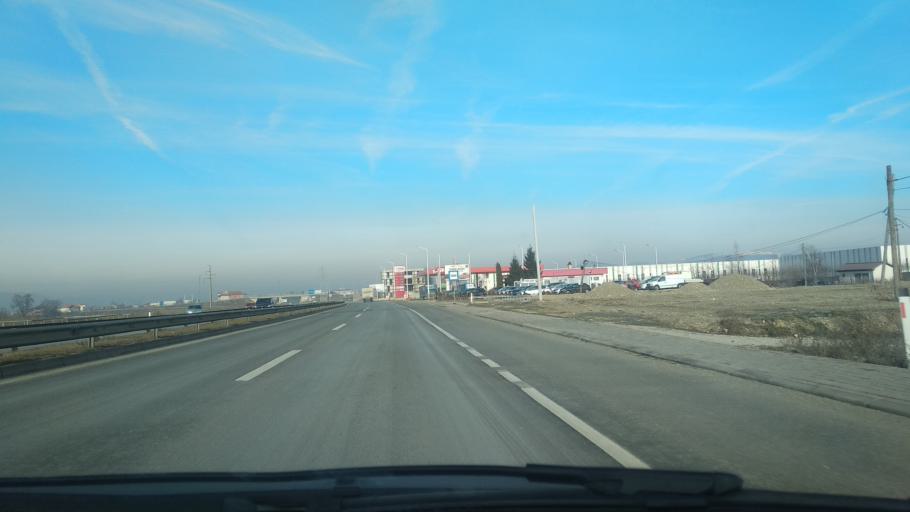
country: XK
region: Pristina
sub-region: Komuna e Obiliqit
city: Obiliq
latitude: 42.7142
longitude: 21.0979
